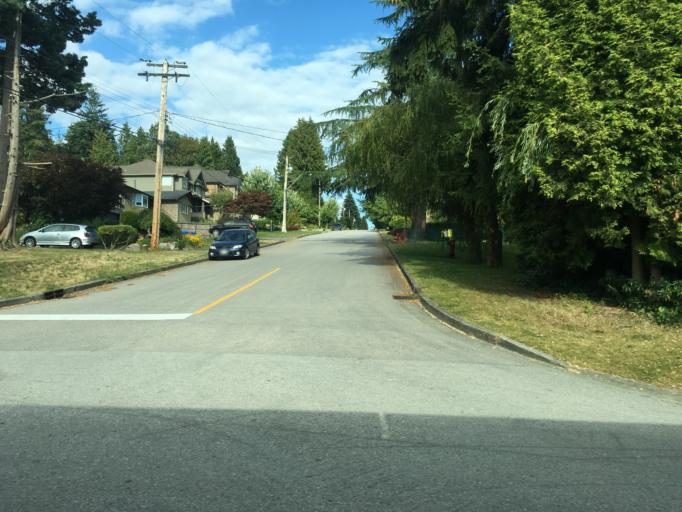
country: CA
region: British Columbia
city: Port Moody
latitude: 49.2482
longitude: -122.8854
